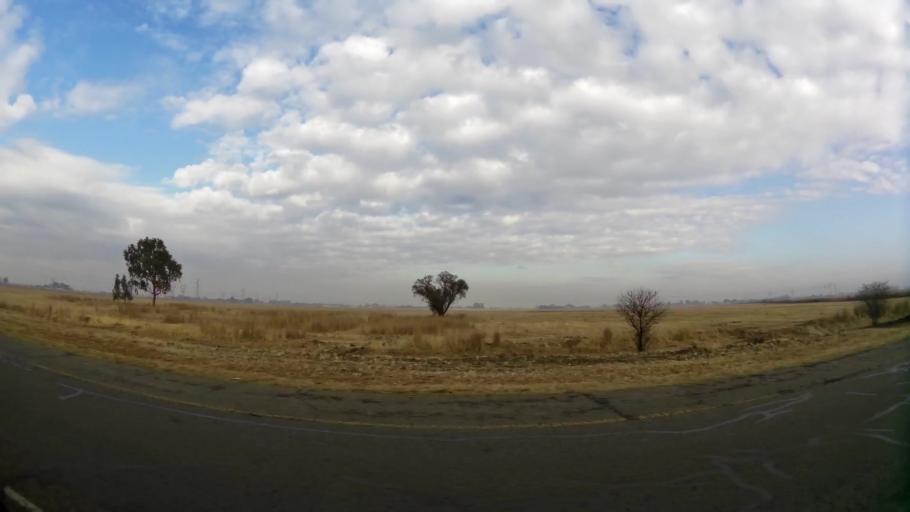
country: ZA
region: Gauteng
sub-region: Sedibeng District Municipality
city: Vanderbijlpark
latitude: -26.6651
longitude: 27.7867
